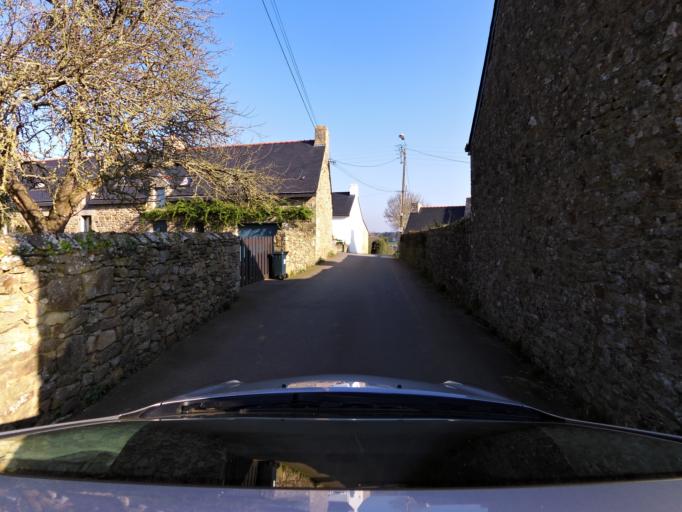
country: FR
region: Brittany
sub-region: Departement du Morbihan
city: Guidel-Plage
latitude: 47.7733
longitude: -3.4920
